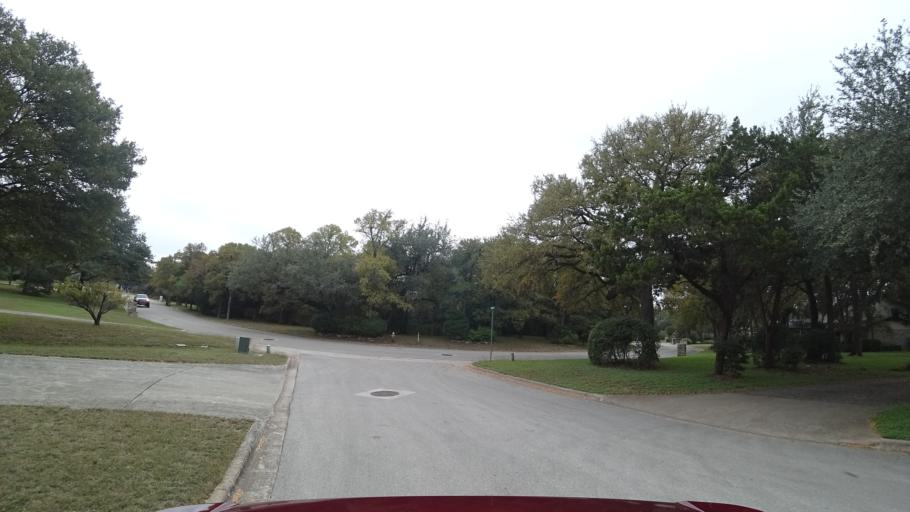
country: US
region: Texas
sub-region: Williamson County
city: Anderson Mill
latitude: 30.4479
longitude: -97.8151
